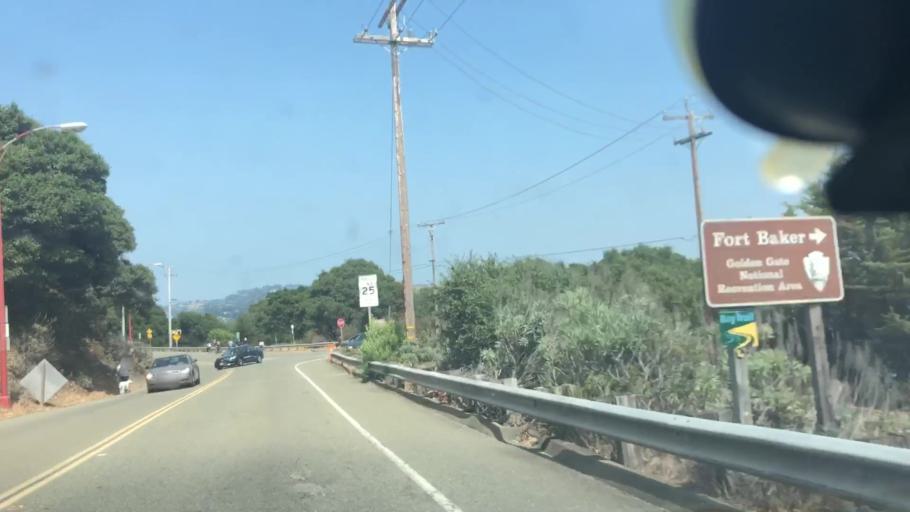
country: US
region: California
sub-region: Marin County
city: Sausalito
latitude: 37.8441
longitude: -122.4781
